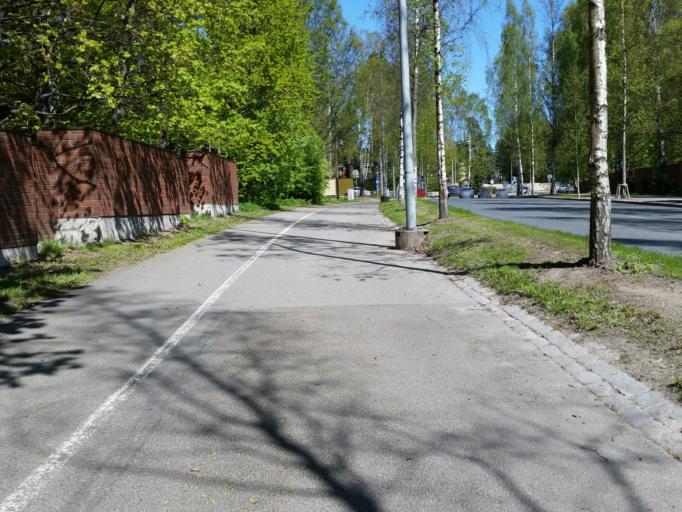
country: FI
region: Uusimaa
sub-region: Helsinki
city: Teekkarikylae
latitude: 60.1838
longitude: 24.8560
